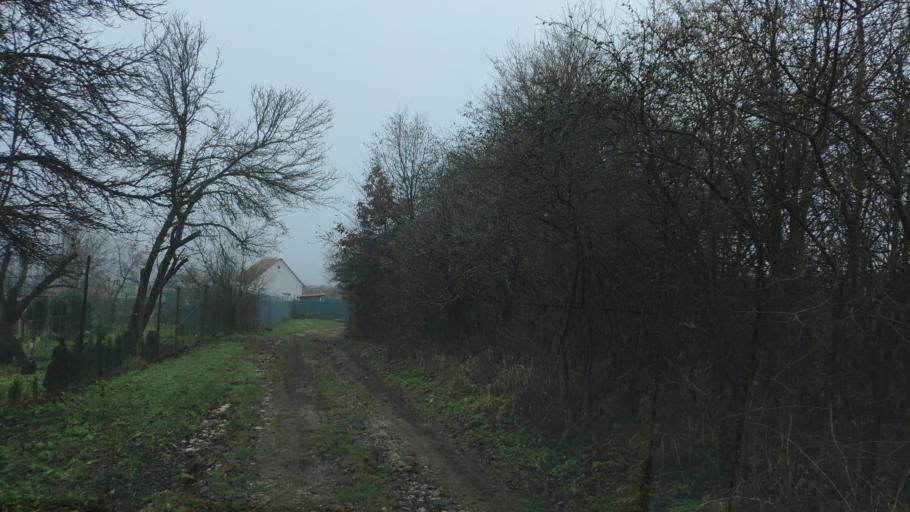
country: SK
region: Banskobystricky
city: Revuca
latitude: 48.6530
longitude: 20.2576
